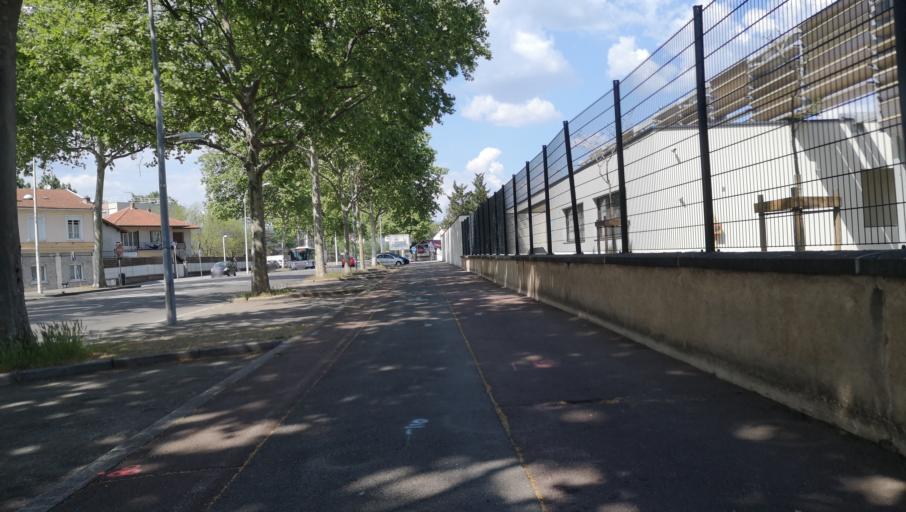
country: FR
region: Rhone-Alpes
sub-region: Departement du Rhone
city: Venissieux
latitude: 45.7274
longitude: 4.8871
